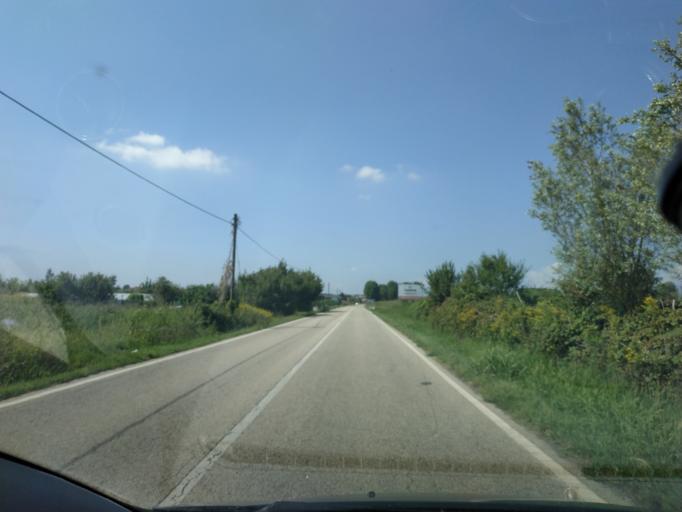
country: IT
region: Piedmont
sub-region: Provincia di Torino
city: San Benigno Canavese
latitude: 45.2341
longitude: 7.7944
